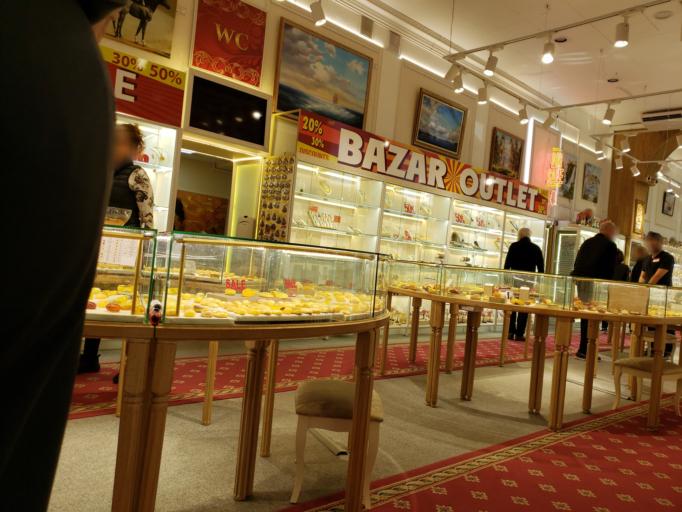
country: RU
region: St.-Petersburg
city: Saint Petersburg
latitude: 59.9537
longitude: 30.3302
